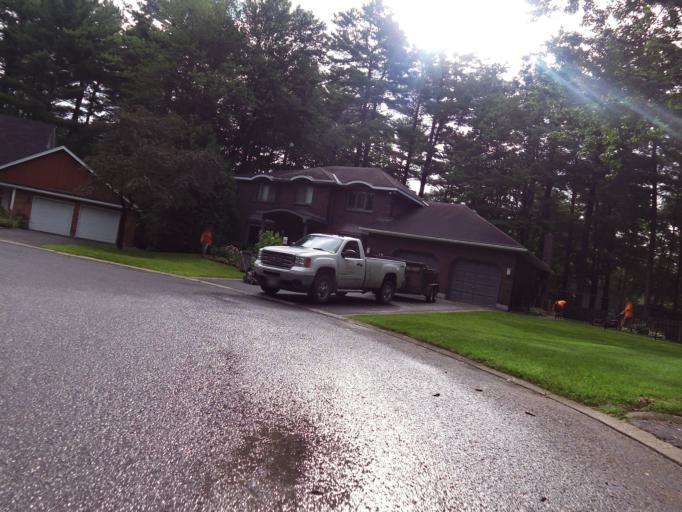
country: CA
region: Ontario
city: Bells Corners
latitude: 45.3240
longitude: -75.7884
